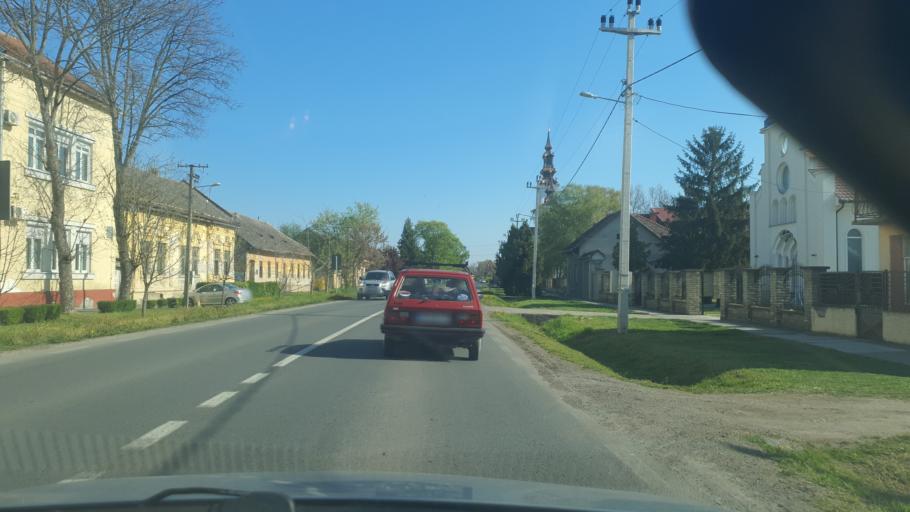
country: RS
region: Autonomna Pokrajina Vojvodina
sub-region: Zapadnobacki Okrug
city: Kula
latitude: 45.6971
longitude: 19.3803
